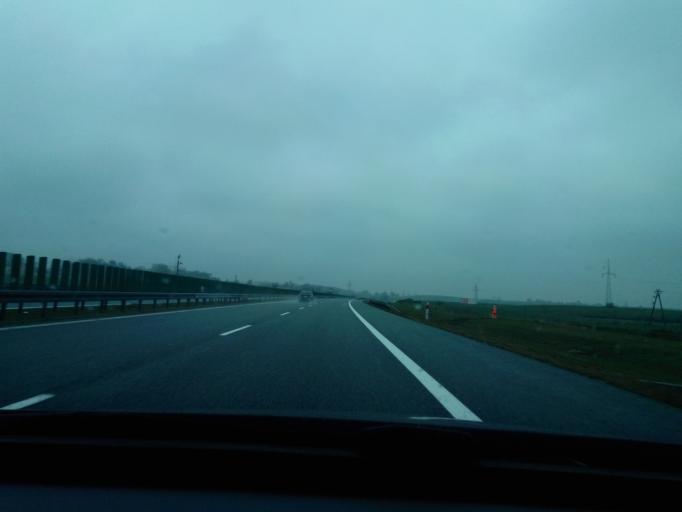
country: PL
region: Pomeranian Voivodeship
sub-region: Powiat gdanski
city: Pszczolki
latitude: 54.1520
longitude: 18.6628
